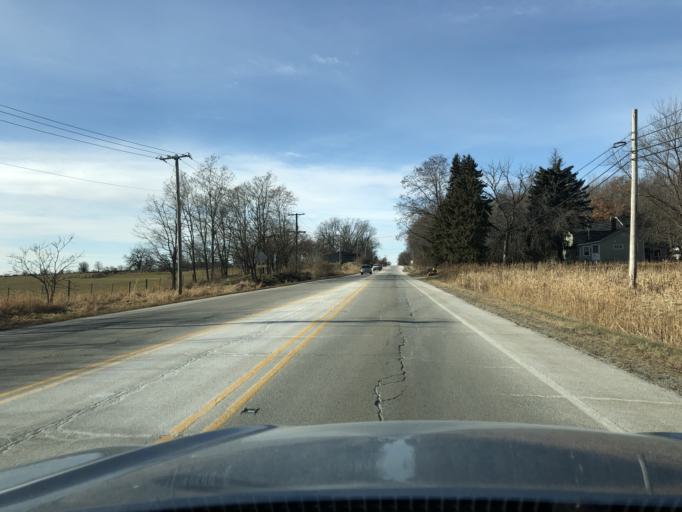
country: US
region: Illinois
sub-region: Lake County
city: Wadsworth
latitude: 42.4658
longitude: -87.9742
